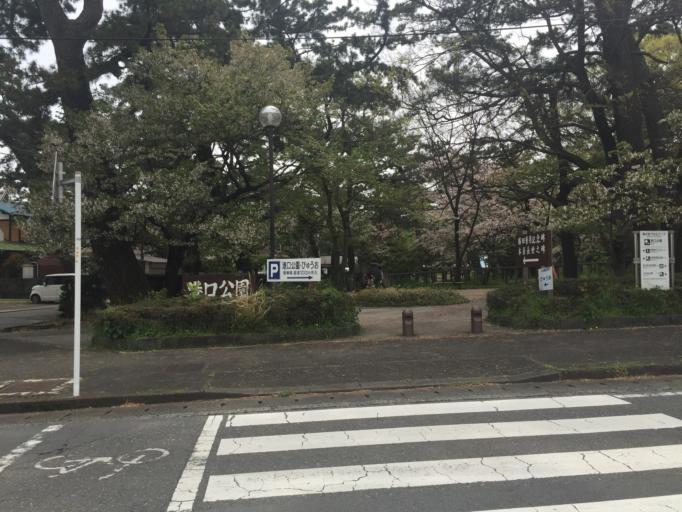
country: JP
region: Shizuoka
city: Numazu
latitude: 35.0836
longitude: 138.8548
